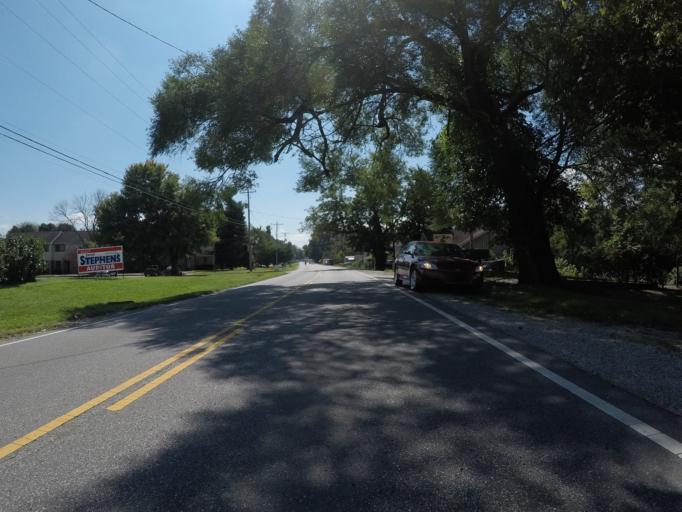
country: US
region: Ohio
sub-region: Lawrence County
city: South Point
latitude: 38.4556
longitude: -82.5962
